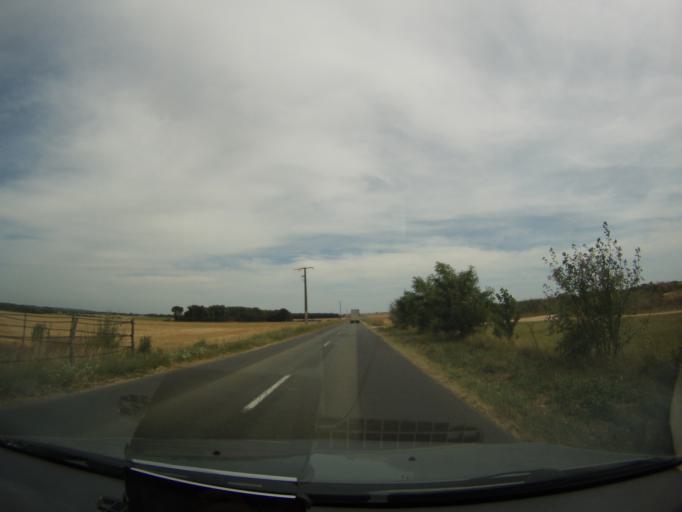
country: FR
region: Poitou-Charentes
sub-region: Departement de la Vienne
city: Mirebeau
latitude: 46.7396
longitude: 0.1843
